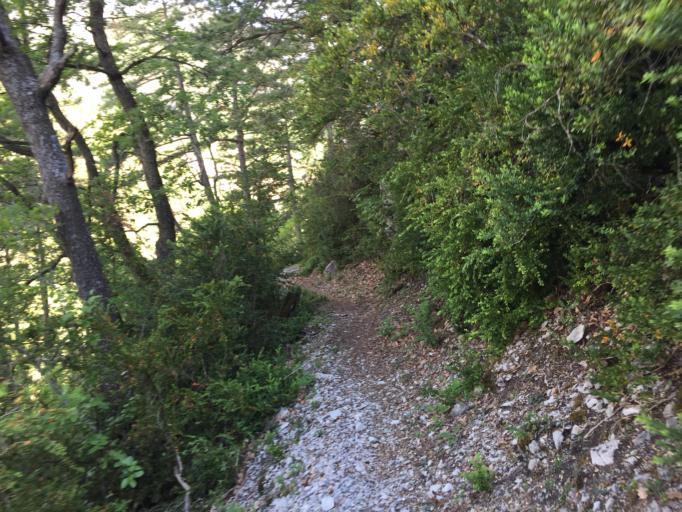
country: FR
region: Provence-Alpes-Cote d'Azur
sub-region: Departement des Alpes-de-Haute-Provence
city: Digne-les-Bains
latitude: 43.9475
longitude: 6.2461
